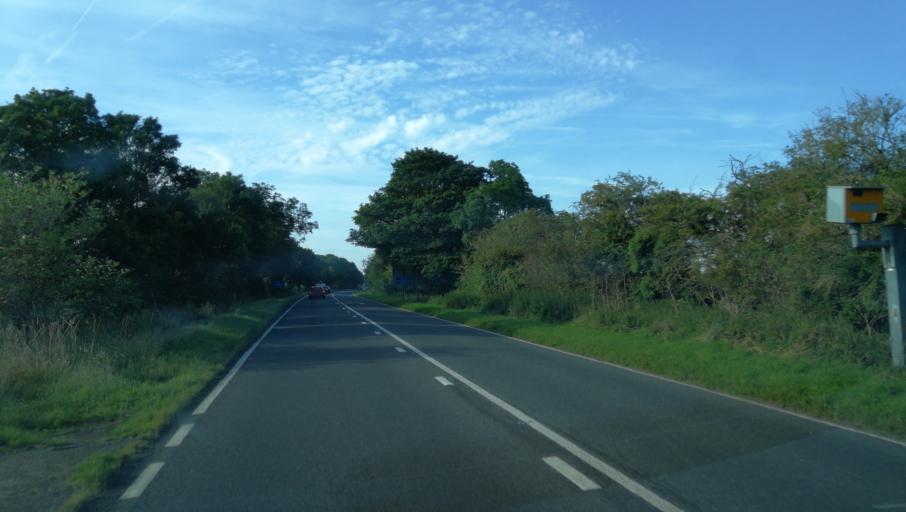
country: GB
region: England
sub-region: Oxfordshire
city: Deddington
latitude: 51.9526
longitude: -1.3185
